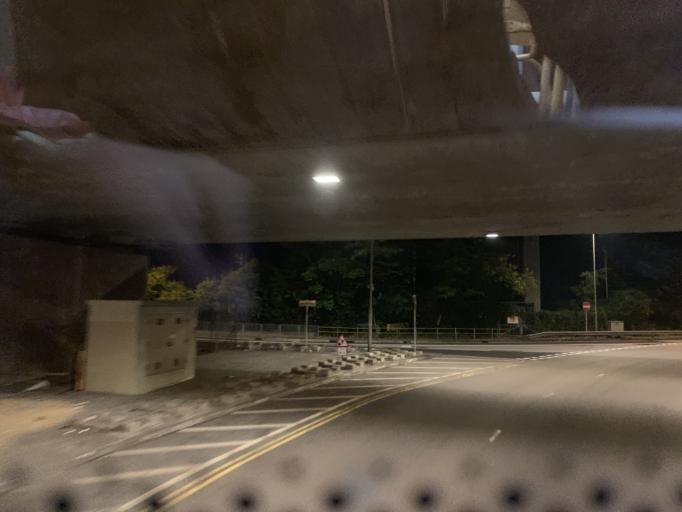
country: HK
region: Tsuen Wan
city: Tsuen Wan
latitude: 22.3596
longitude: 114.1033
